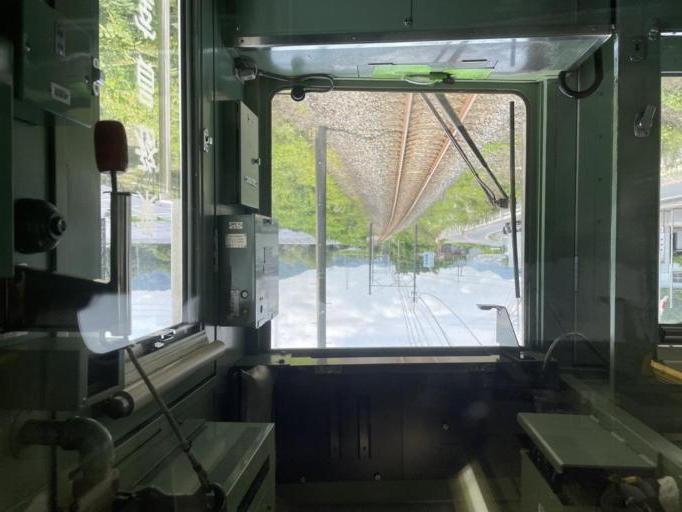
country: JP
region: Tochigi
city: Tanuma
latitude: 36.3857
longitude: 139.5995
